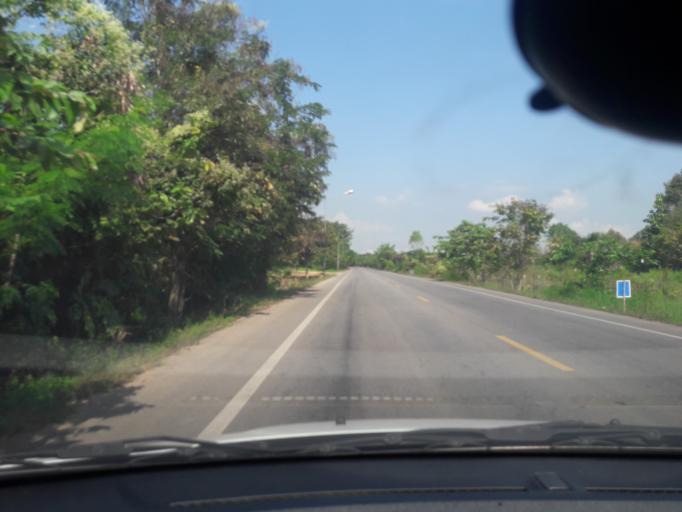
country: TH
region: Lampang
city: Lampang
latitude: 18.2179
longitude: 99.4921
